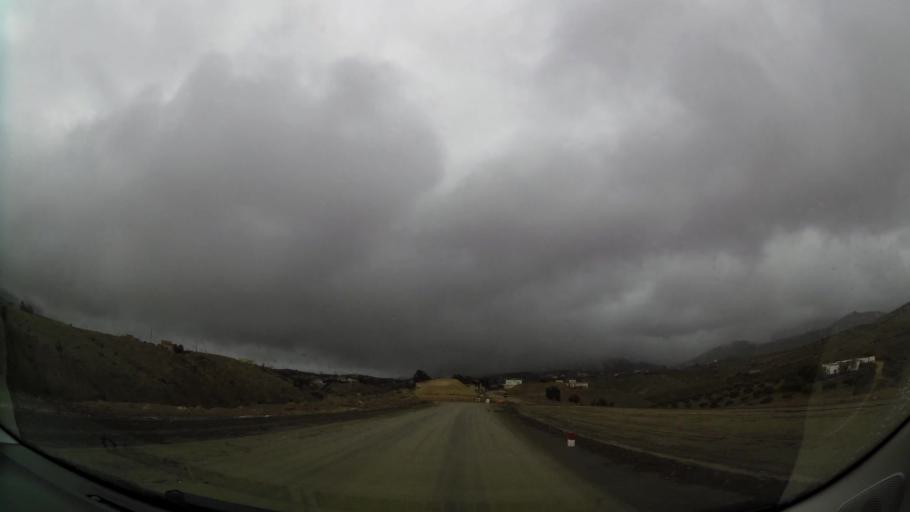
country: MA
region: Oriental
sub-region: Nador
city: Midar
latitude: 34.8935
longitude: -3.7655
